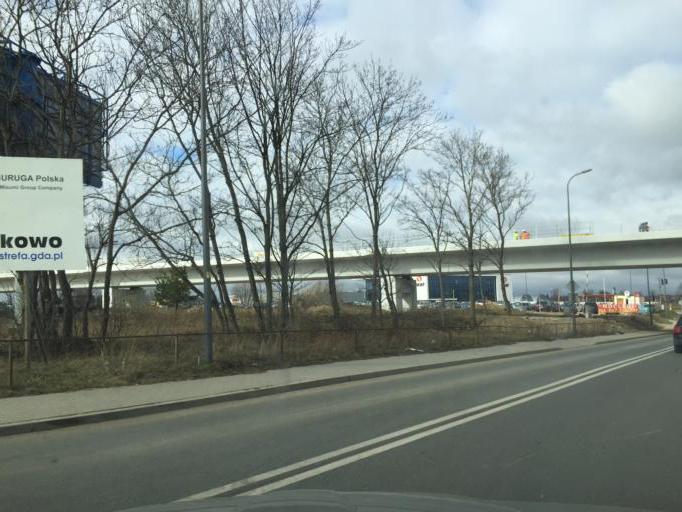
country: PL
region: Pomeranian Voivodeship
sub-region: Powiat kartuski
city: Banino
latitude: 54.3813
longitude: 18.4749
